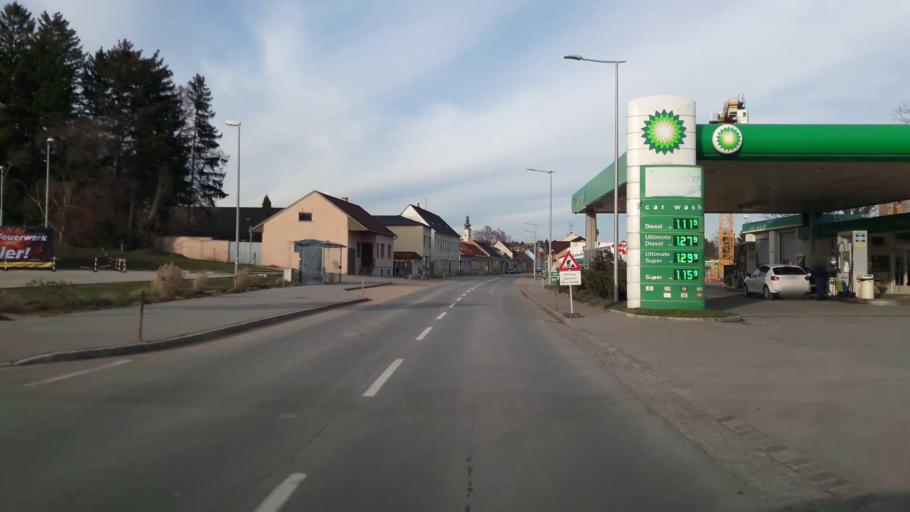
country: AT
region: Lower Austria
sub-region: Politischer Bezirk Mistelbach
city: Gaweinstal
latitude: 48.4720
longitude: 16.5889
